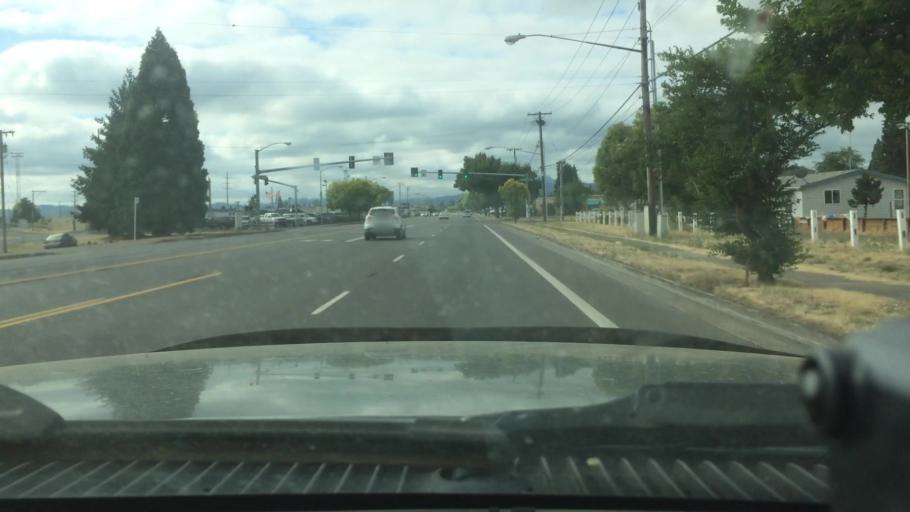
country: US
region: Oregon
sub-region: Lane County
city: Eugene
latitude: 44.0812
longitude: -123.1523
